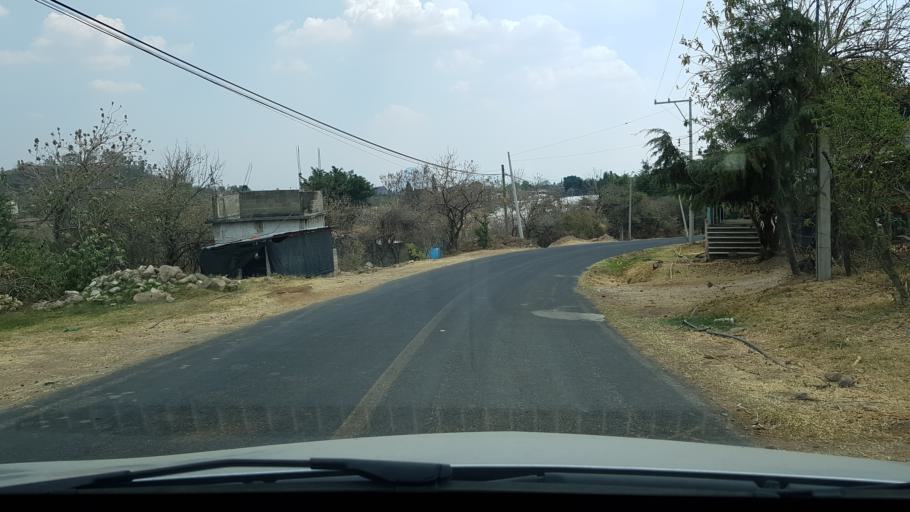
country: MX
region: Morelos
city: Tlacotepec
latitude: 18.8209
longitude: -98.7430
